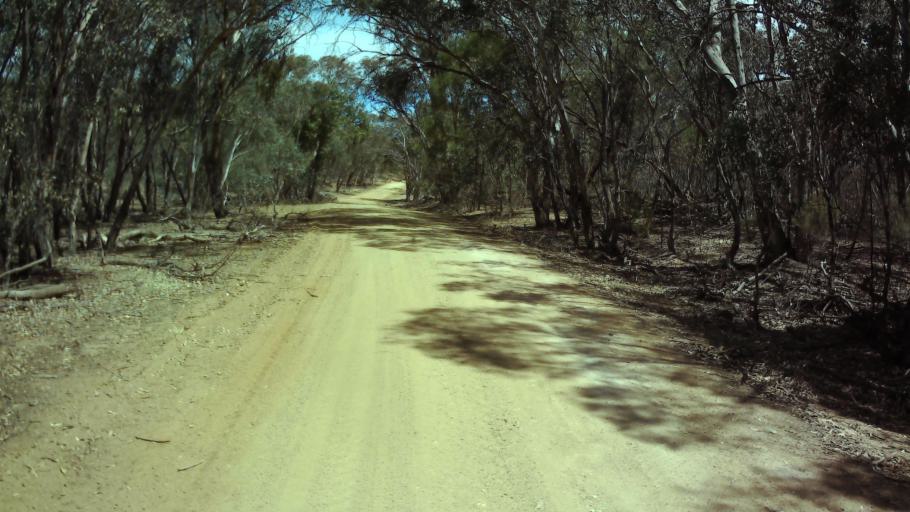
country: AU
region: New South Wales
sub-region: Weddin
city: Grenfell
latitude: -33.8033
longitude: 148.1602
